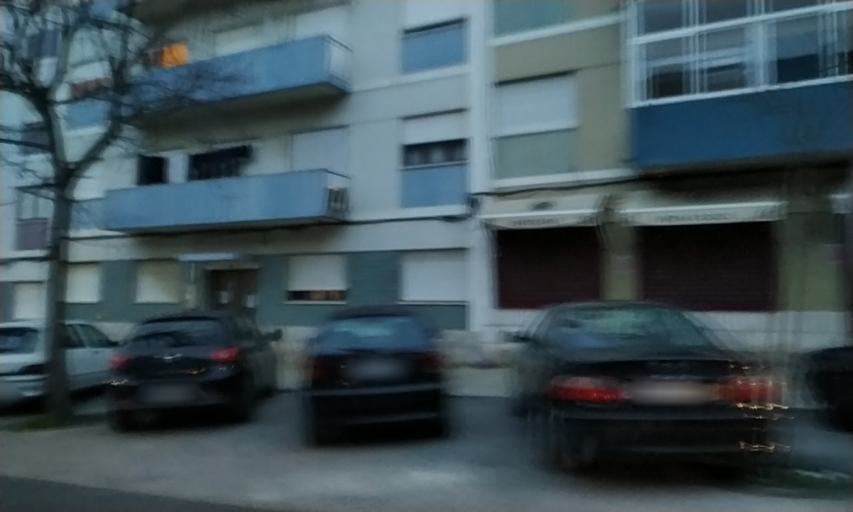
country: PT
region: Setubal
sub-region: Setubal
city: Setubal
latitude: 38.5283
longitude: -8.8754
